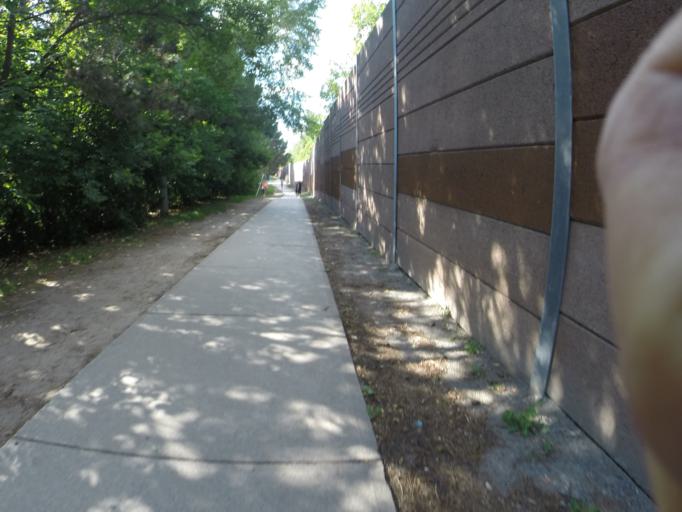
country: CA
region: Ontario
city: Toronto
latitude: 43.7029
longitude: -79.4370
